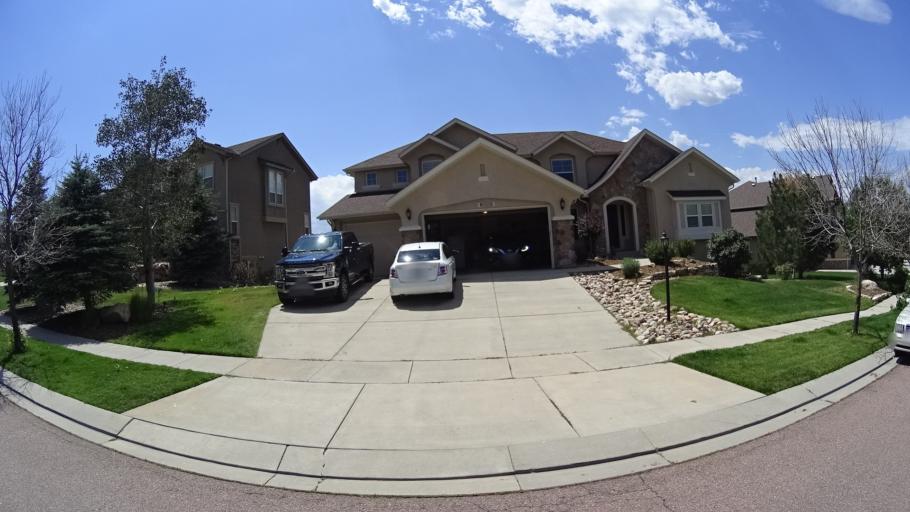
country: US
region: Colorado
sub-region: El Paso County
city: Black Forest
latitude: 38.9709
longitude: -104.7600
